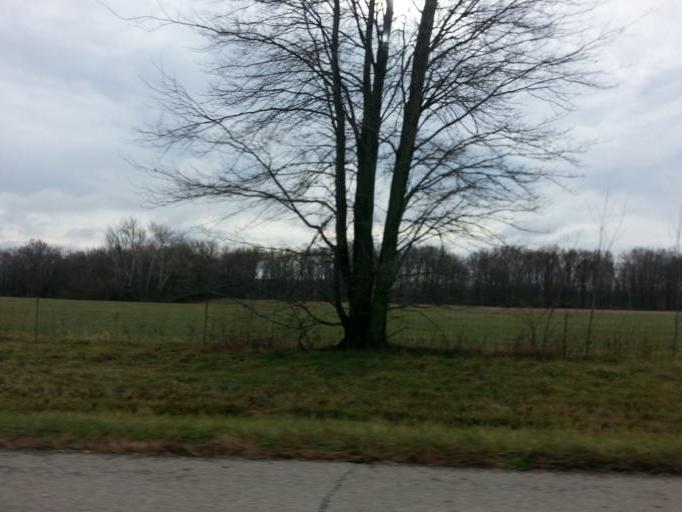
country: US
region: Indiana
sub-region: Ripley County
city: Batesville
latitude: 39.3153
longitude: -85.2541
